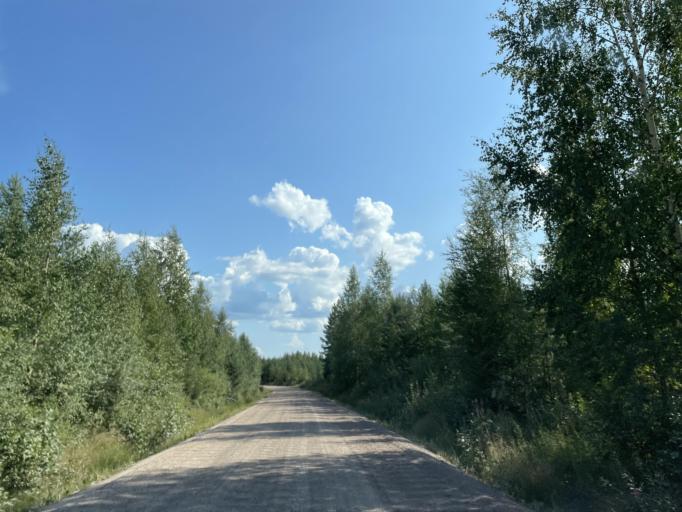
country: FI
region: Central Finland
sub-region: Saarijaervi-Viitasaari
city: Pihtipudas
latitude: 63.3476
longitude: 25.7902
